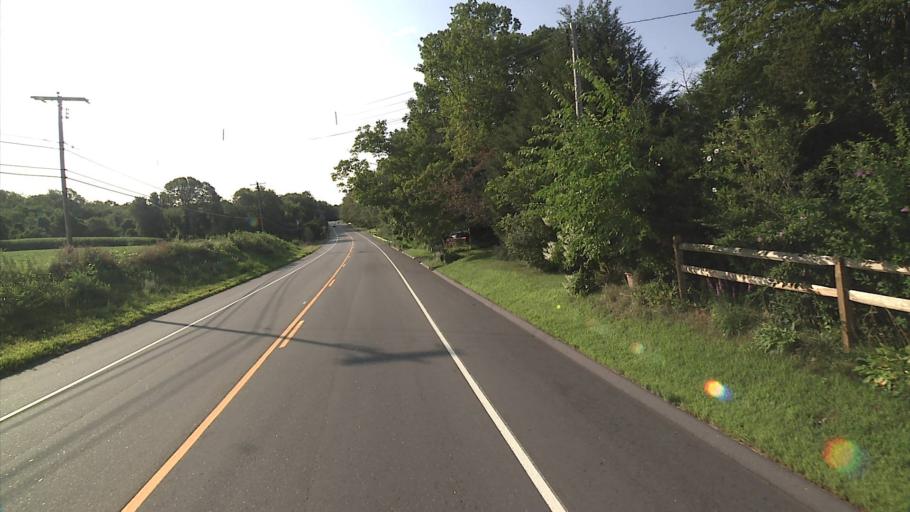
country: US
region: Connecticut
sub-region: New London County
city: Norwich
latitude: 41.5037
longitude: -72.0392
